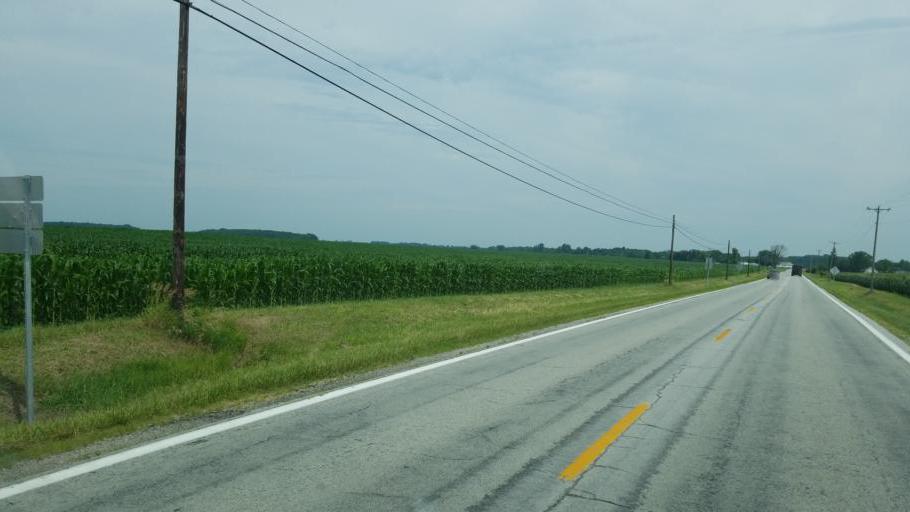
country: US
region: Ohio
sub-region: Madison County
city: Choctaw Lake
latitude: 39.9943
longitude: -83.4204
